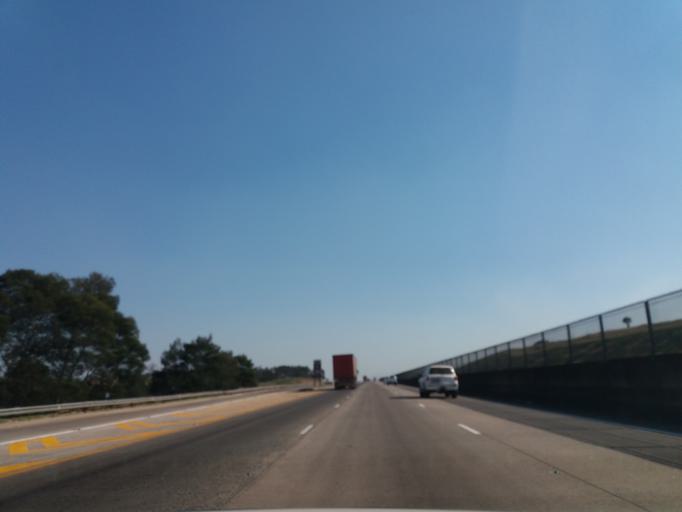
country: ZA
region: KwaZulu-Natal
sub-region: eThekwini Metropolitan Municipality
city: Mpumalanga
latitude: -29.7389
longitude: 30.6391
